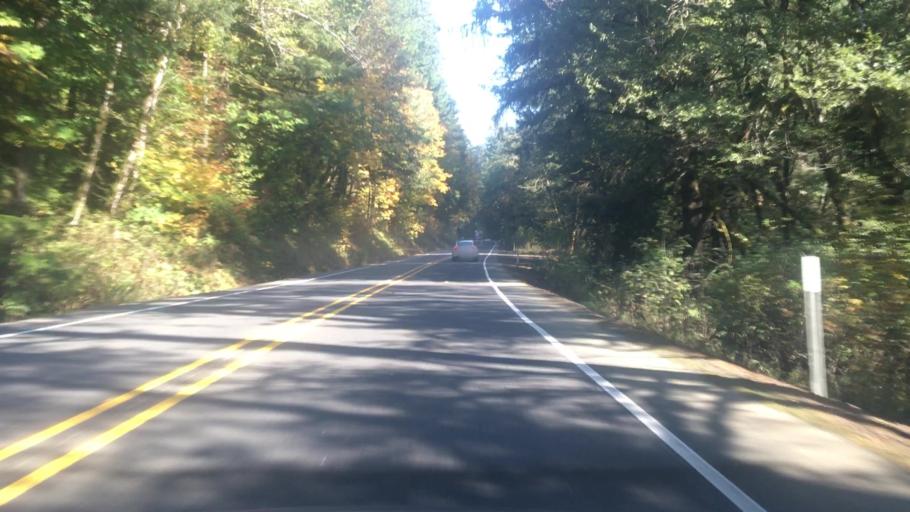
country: US
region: Oregon
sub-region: Lincoln County
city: Rose Lodge
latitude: 45.0524
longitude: -123.7765
